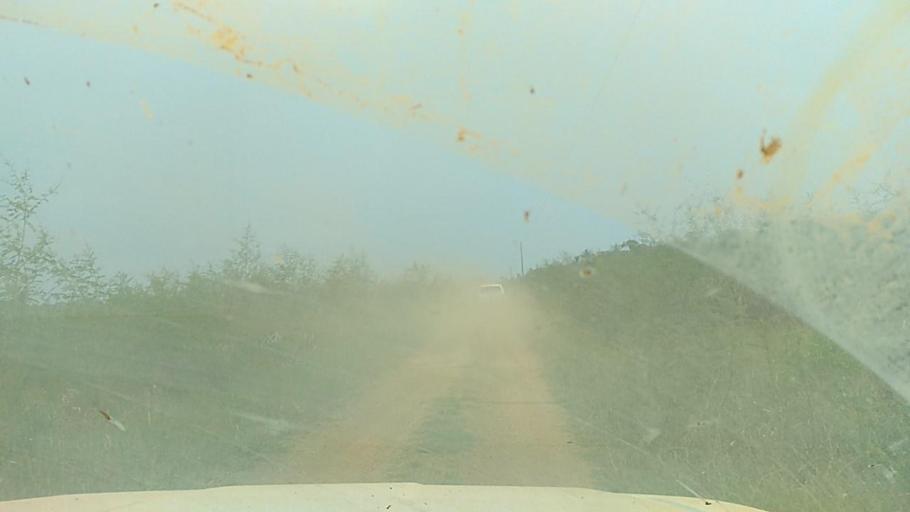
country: BR
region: Rondonia
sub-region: Porto Velho
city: Porto Velho
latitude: -8.9759
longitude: -64.3845
